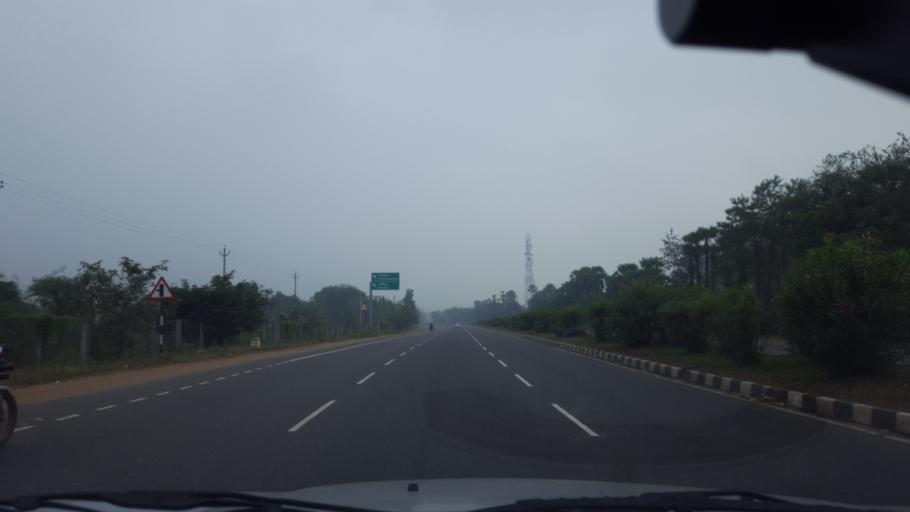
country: IN
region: Andhra Pradesh
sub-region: Prakasam
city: Addanki
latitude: 15.8351
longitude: 80.0480
